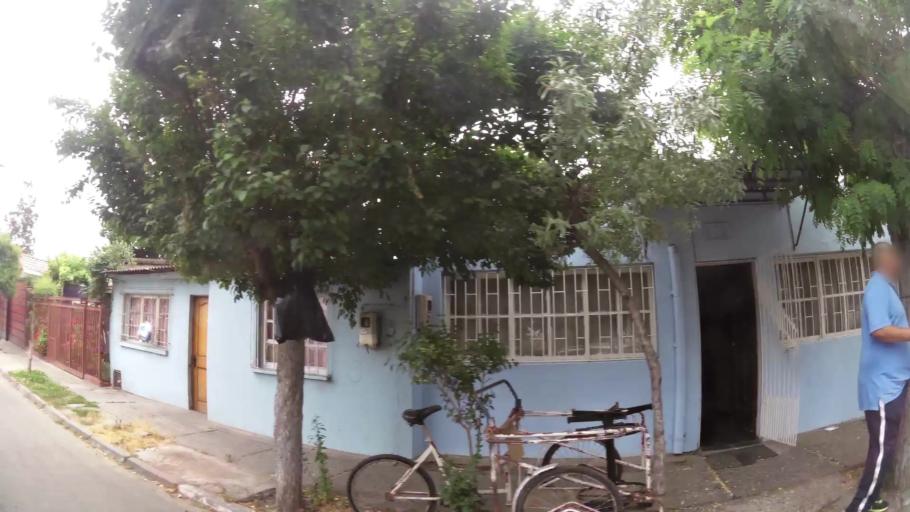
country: CL
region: Santiago Metropolitan
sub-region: Provincia de Santiago
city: Santiago
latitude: -33.5111
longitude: -70.6896
